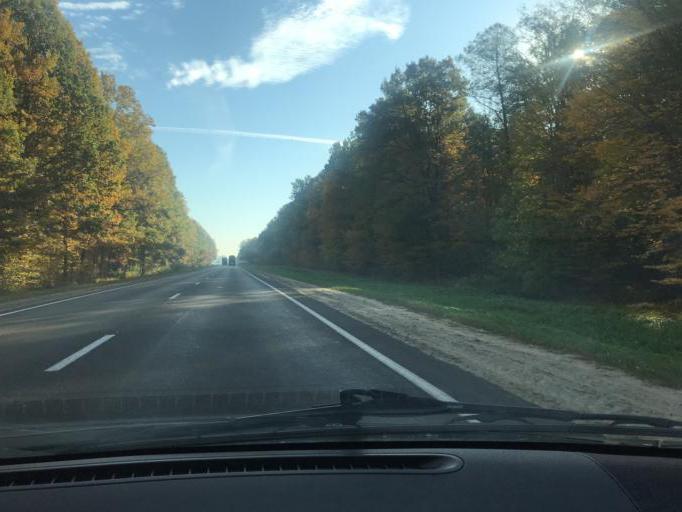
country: BY
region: Brest
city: Ivanava
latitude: 52.1525
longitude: 25.3644
